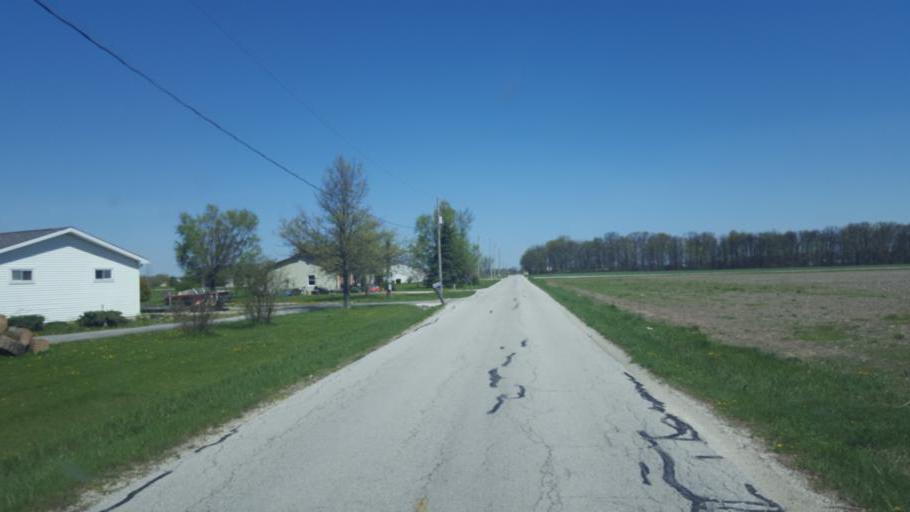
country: US
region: Ohio
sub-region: Ottawa County
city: Oak Harbor
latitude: 41.4631
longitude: -83.1258
